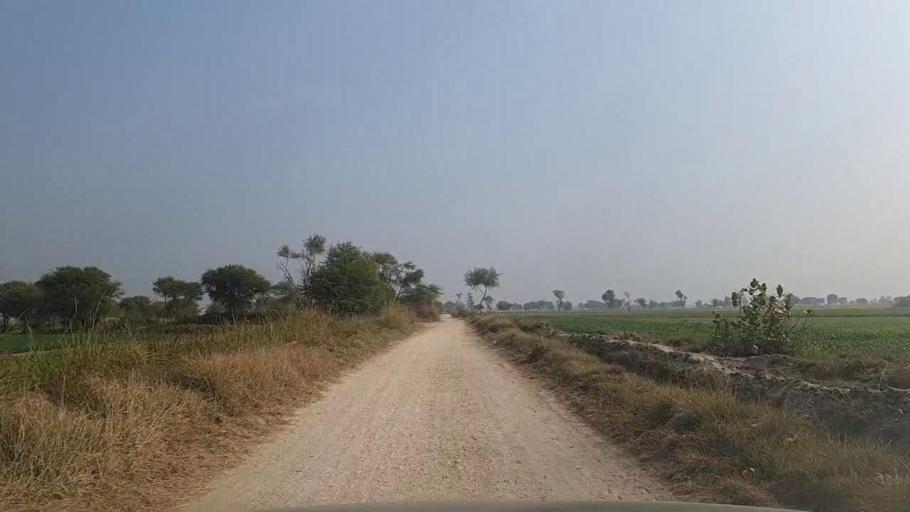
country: PK
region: Sindh
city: Nawabshah
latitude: 26.2887
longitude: 68.4439
